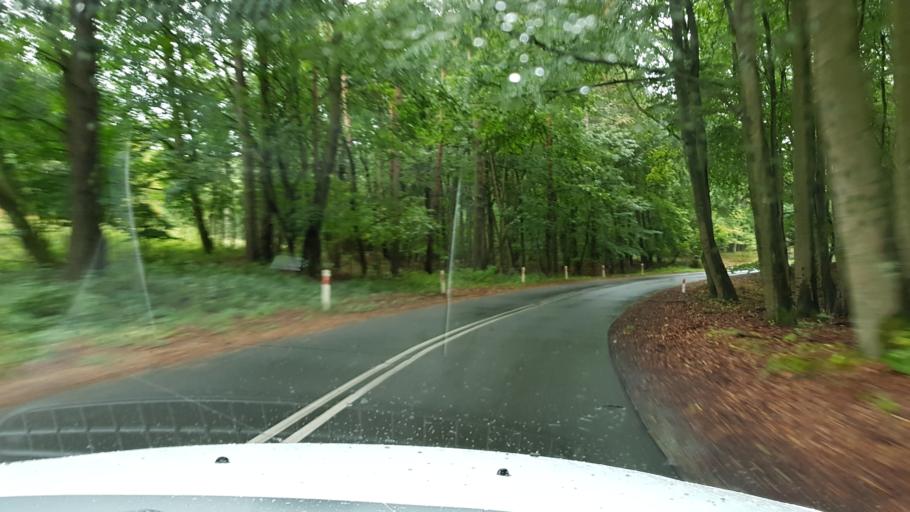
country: PL
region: West Pomeranian Voivodeship
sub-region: Powiat gryfinski
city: Cedynia
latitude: 52.9268
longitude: 14.1819
